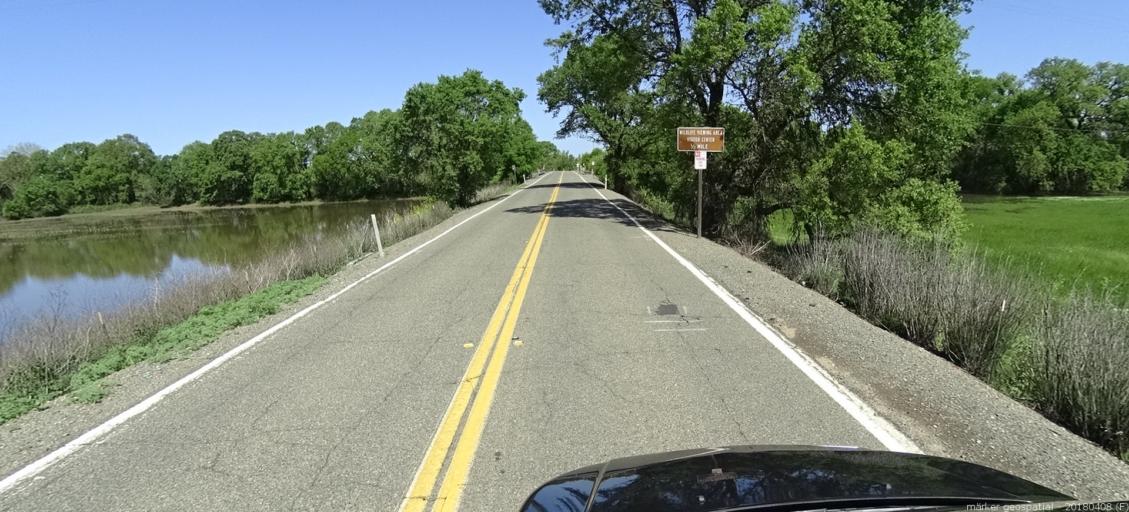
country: US
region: California
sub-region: San Joaquin County
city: Thornton
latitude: 38.2618
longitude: -121.4407
